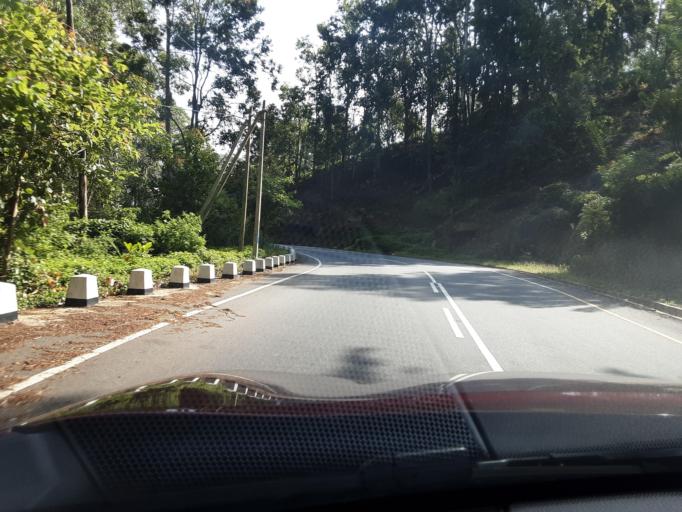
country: LK
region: Uva
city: Badulla
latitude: 6.9595
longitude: 81.1089
